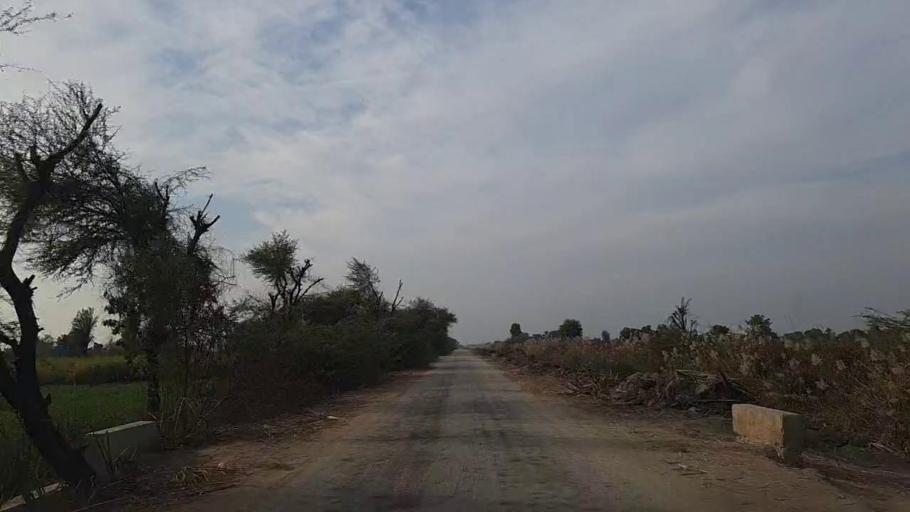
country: PK
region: Sindh
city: Daur
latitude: 26.4958
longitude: 68.4516
